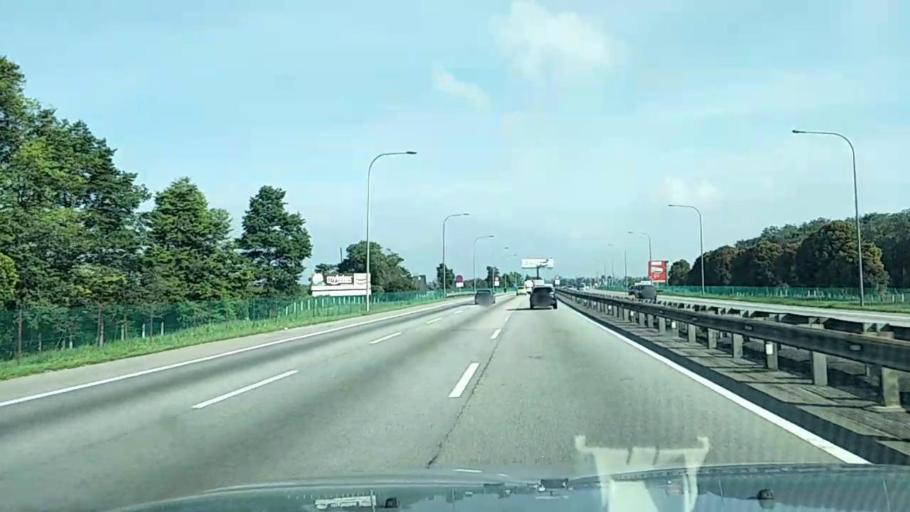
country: MY
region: Putrajaya
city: Putrajaya
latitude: 2.8807
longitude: 101.6274
